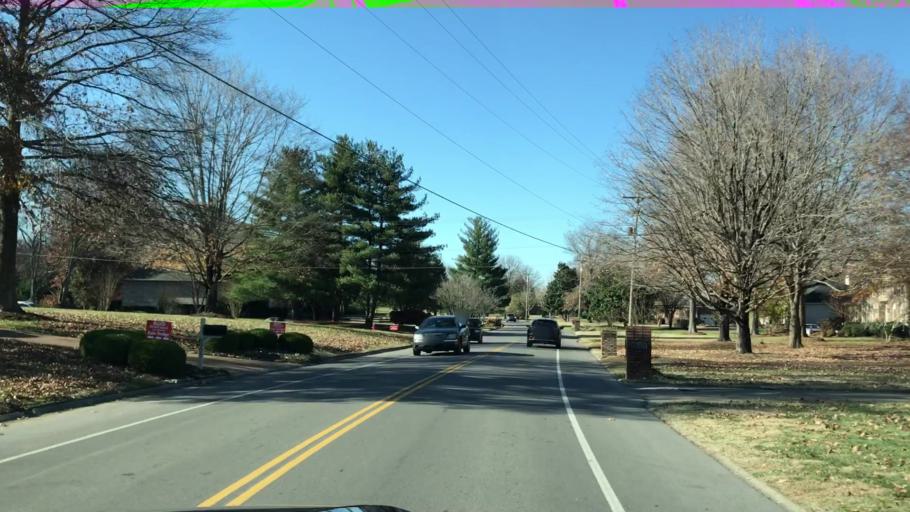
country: US
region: Tennessee
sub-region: Williamson County
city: Brentwood
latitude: 36.0245
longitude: -86.8209
